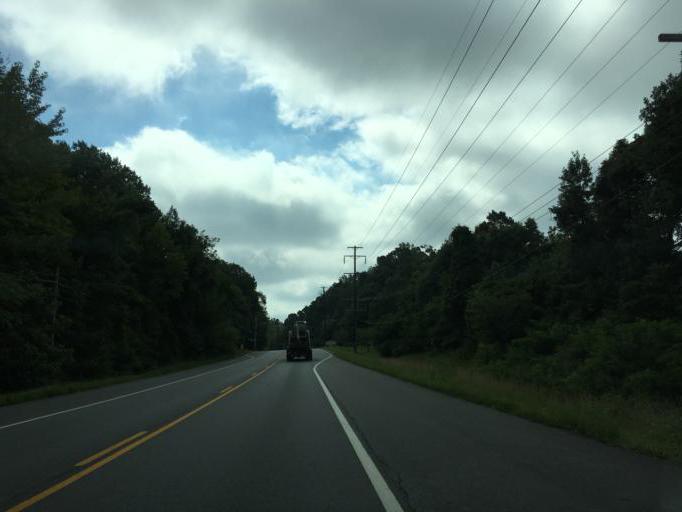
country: US
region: Maryland
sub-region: Anne Arundel County
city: Crownsville
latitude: 39.0174
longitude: -76.5814
